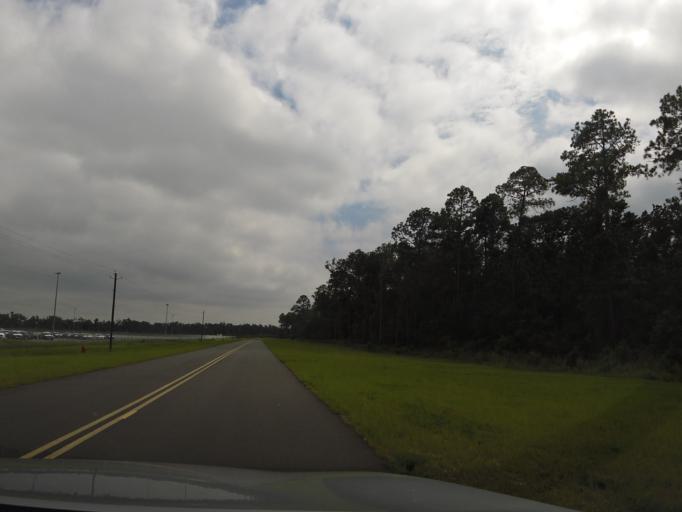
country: US
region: Georgia
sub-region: Glynn County
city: Brunswick
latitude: 31.1114
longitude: -81.5461
